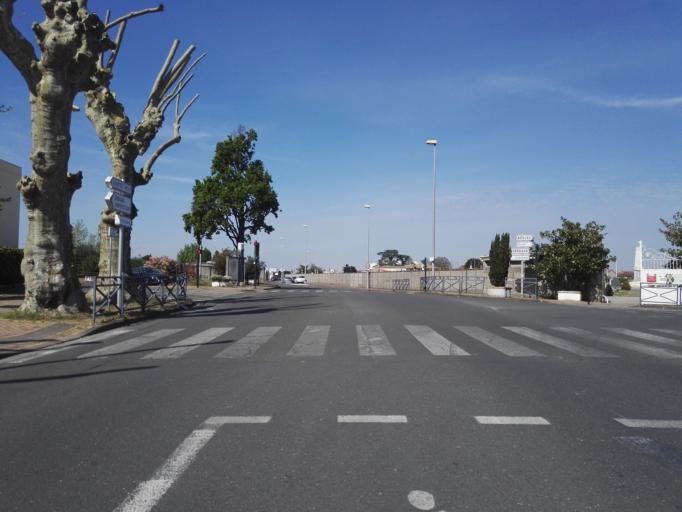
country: FR
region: Aquitaine
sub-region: Departement de la Gironde
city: Talence
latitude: 44.8118
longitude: -0.5822
